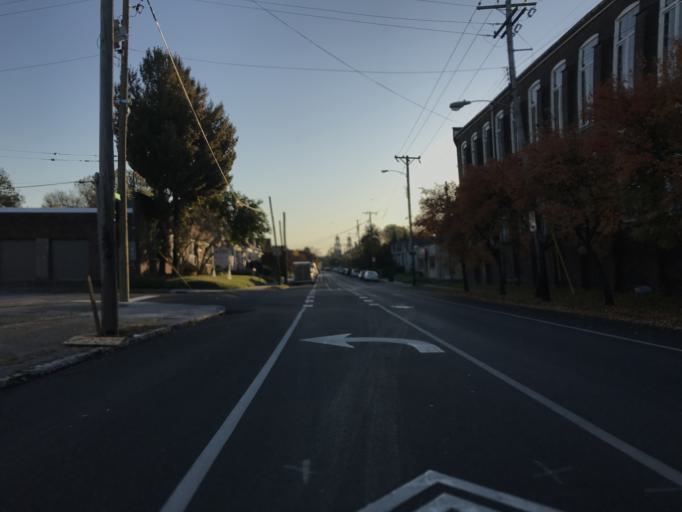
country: US
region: Kentucky
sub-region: Jefferson County
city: Louisville
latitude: 38.2361
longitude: -85.7375
